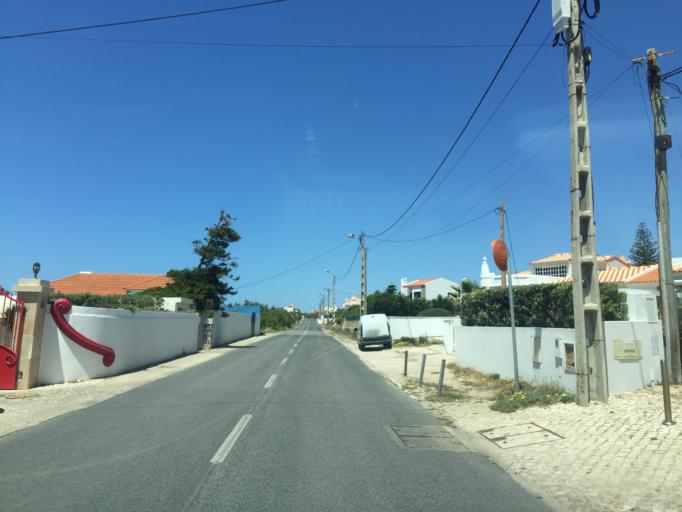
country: PT
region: Lisbon
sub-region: Sintra
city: Colares
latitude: 38.8319
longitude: -9.4674
